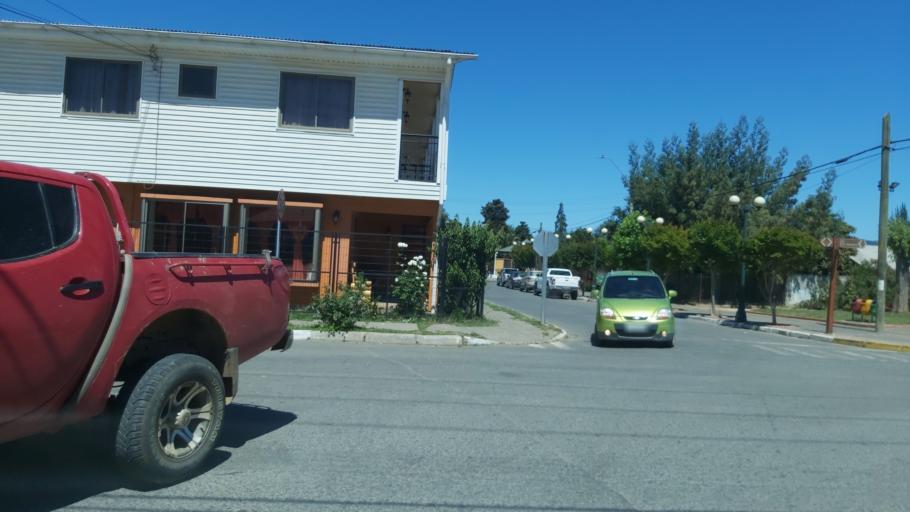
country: CL
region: Maule
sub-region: Provincia de Talca
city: Talca
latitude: -34.9851
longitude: -71.9831
